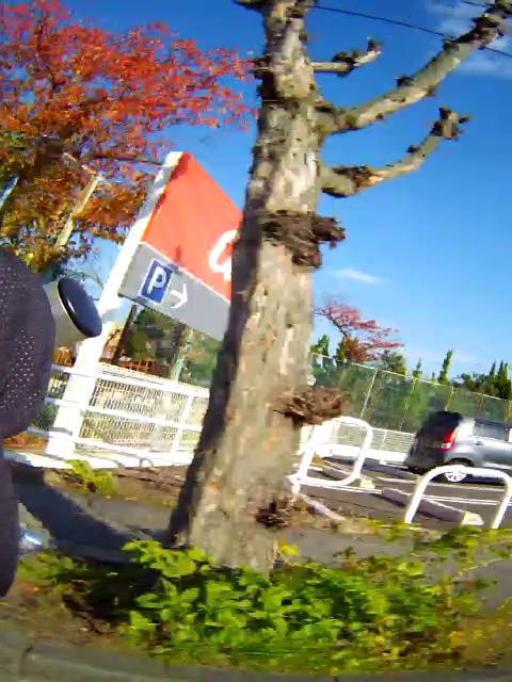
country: JP
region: Hyogo
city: Takarazuka
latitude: 34.7905
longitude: 135.3569
